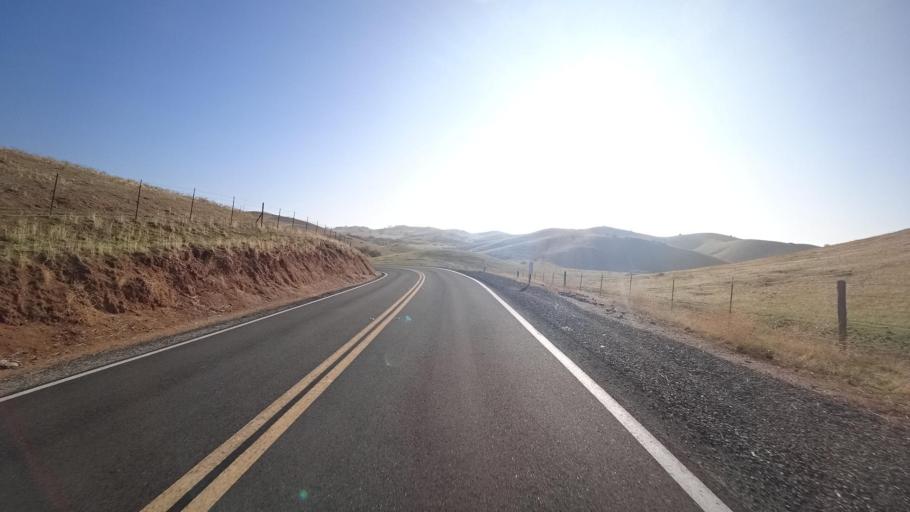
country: US
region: California
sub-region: Tulare County
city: Richgrove
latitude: 35.7418
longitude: -118.8871
